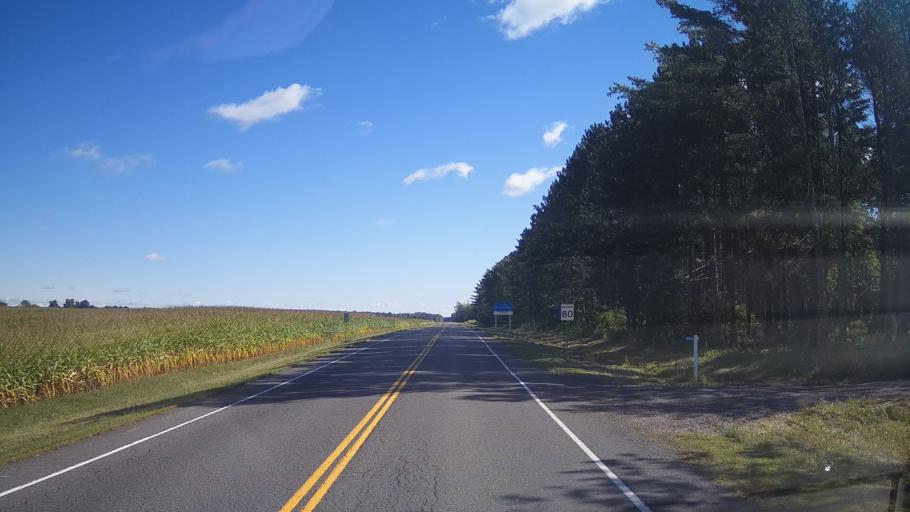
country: CA
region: Ontario
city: Prescott
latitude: 44.9044
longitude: -75.4431
